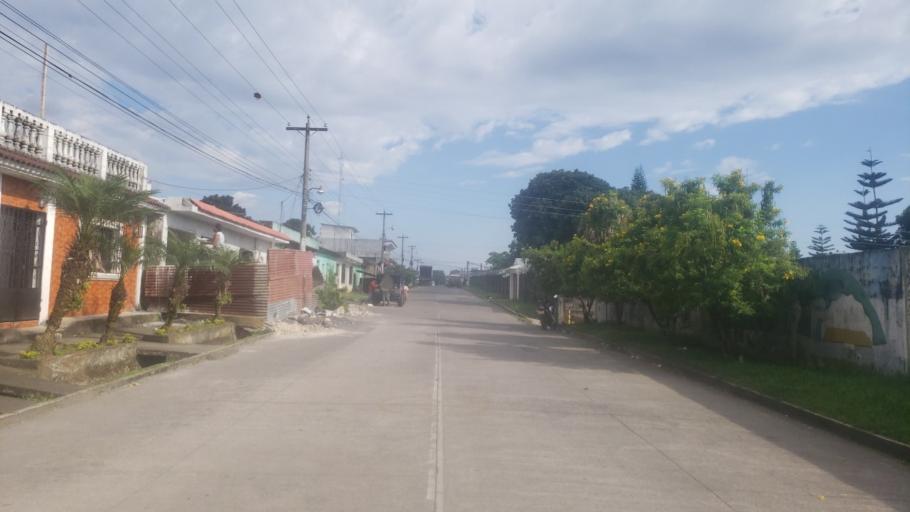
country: GT
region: Suchitepeque
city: Pueblo Nuevo
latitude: 14.6479
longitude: -91.5560
